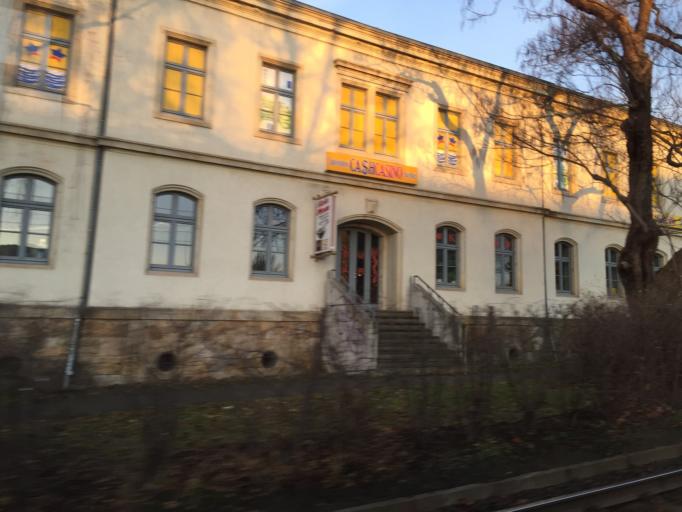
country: DE
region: Saxony
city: Albertstadt
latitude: 51.0810
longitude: 13.7595
